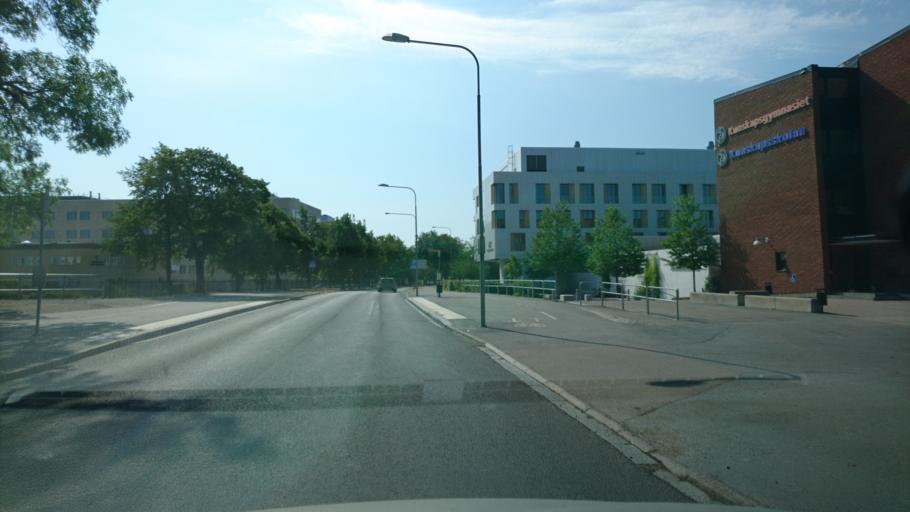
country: SE
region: Uppsala
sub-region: Uppsala Kommun
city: Uppsala
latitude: 59.8493
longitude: 17.6361
